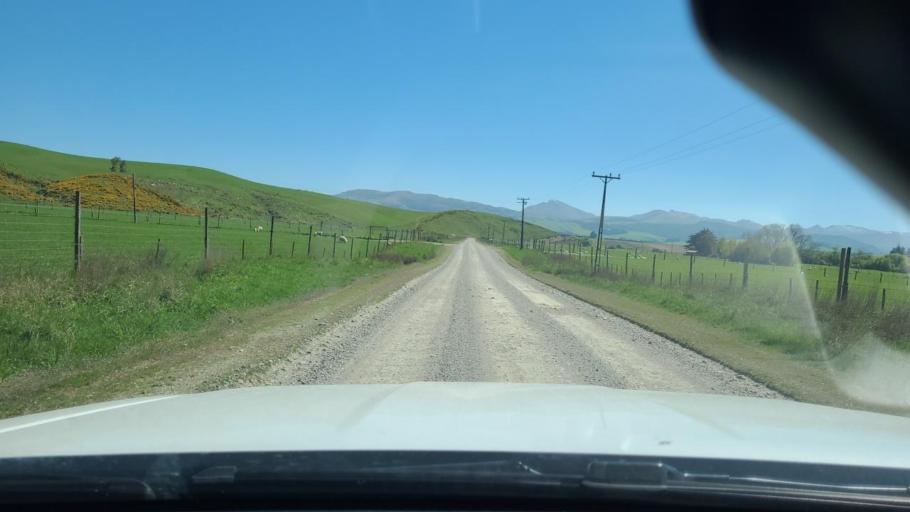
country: NZ
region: Southland
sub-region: Gore District
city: Gore
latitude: -45.7371
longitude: 168.8124
